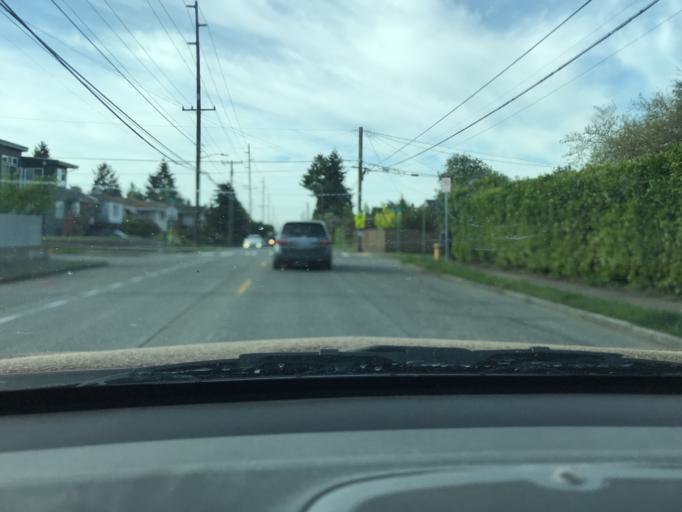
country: US
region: Washington
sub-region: King County
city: Shoreline
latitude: 47.6926
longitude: -122.3231
